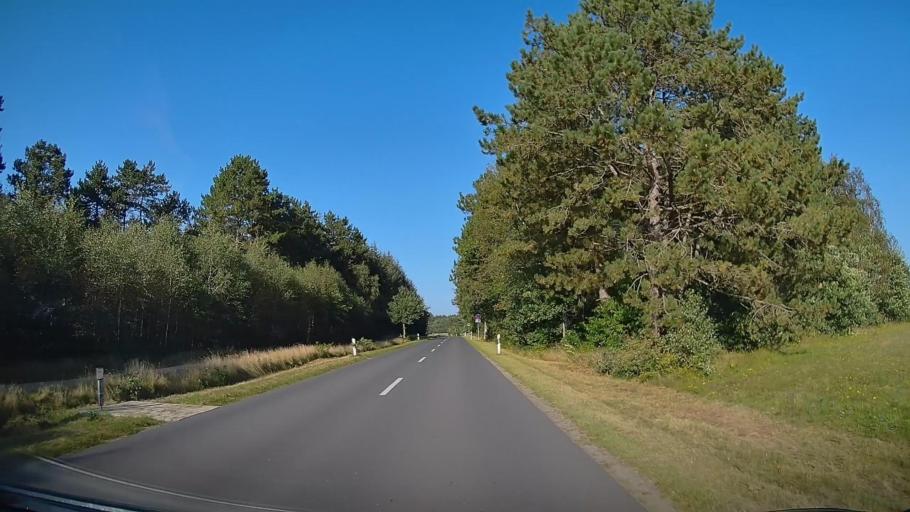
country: DE
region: Lower Saxony
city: Nordholz
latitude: 53.8428
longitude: 8.6238
